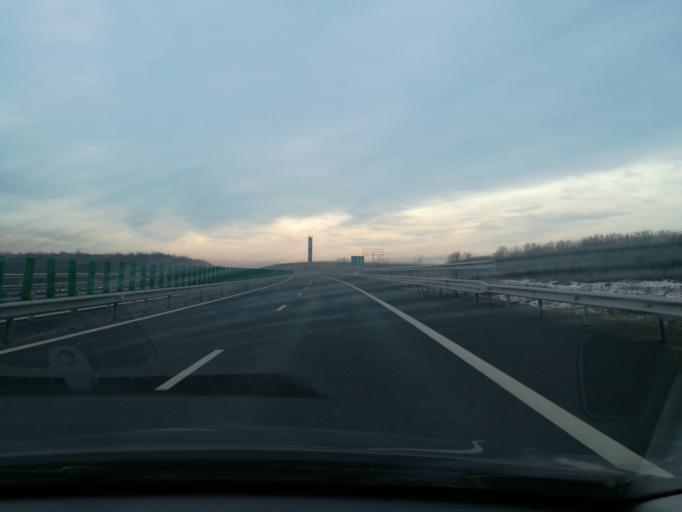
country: RO
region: Constanta
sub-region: Oras Cernavoda
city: Cernavoda
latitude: 44.2953
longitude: 28.0369
